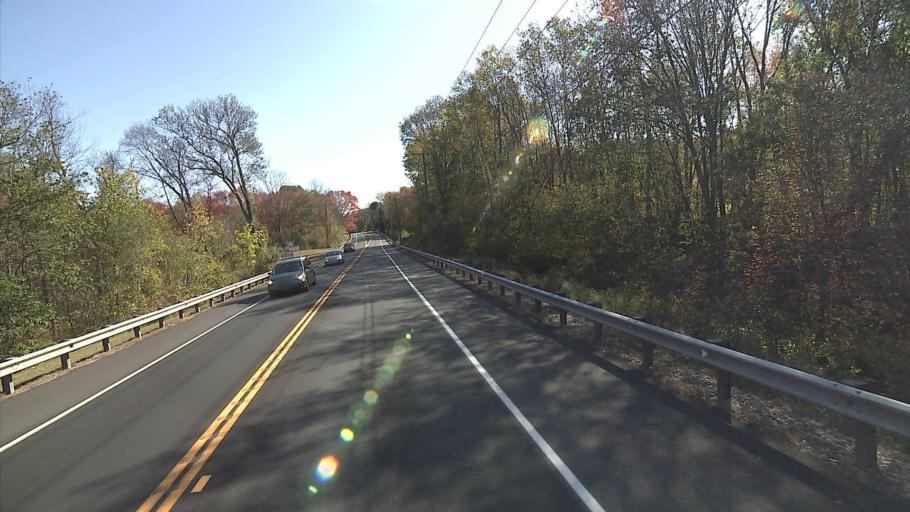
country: US
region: Connecticut
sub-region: Tolland County
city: South Coventry
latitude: 41.7258
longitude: -72.3109
